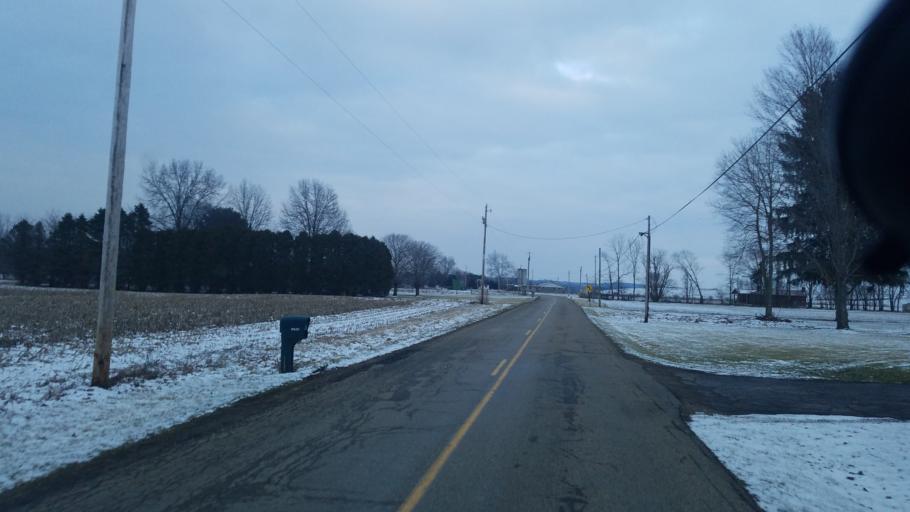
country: US
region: Ohio
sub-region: Knox County
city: Fredericktown
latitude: 40.4239
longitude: -82.5507
